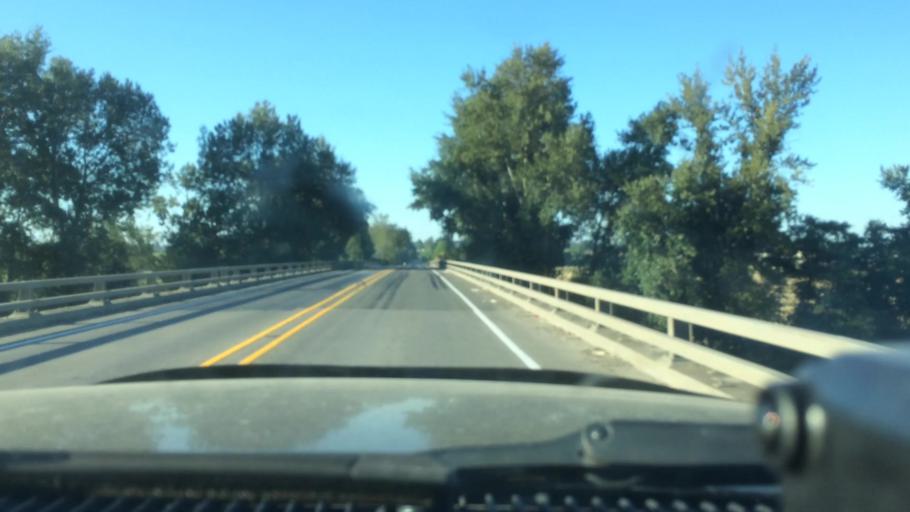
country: US
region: Oregon
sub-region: Yamhill County
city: Newberg
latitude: 45.2678
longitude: -122.9435
